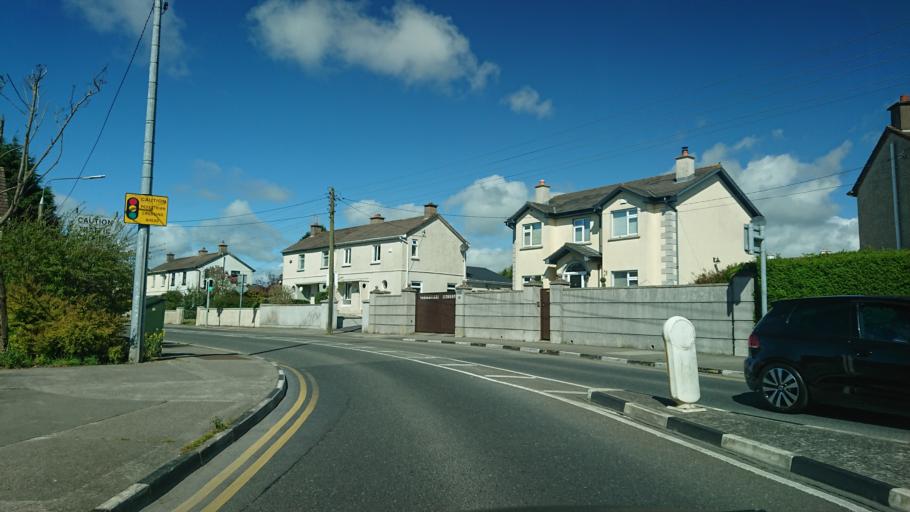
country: IE
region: Munster
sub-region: Waterford
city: Waterford
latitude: 52.2583
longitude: -7.1319
